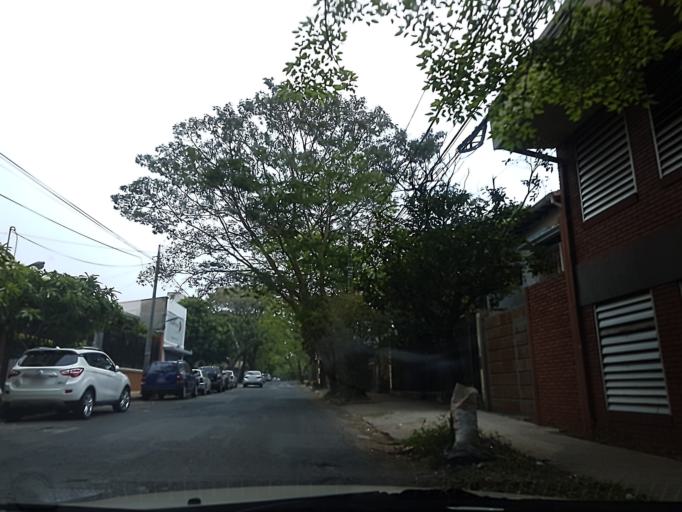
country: PY
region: Asuncion
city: Asuncion
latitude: -25.2944
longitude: -57.5838
